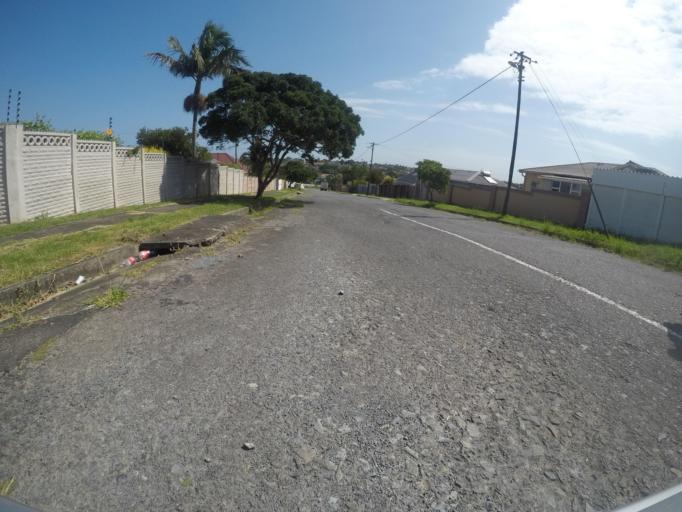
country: ZA
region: Eastern Cape
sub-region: Buffalo City Metropolitan Municipality
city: East London
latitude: -32.9769
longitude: 27.8698
